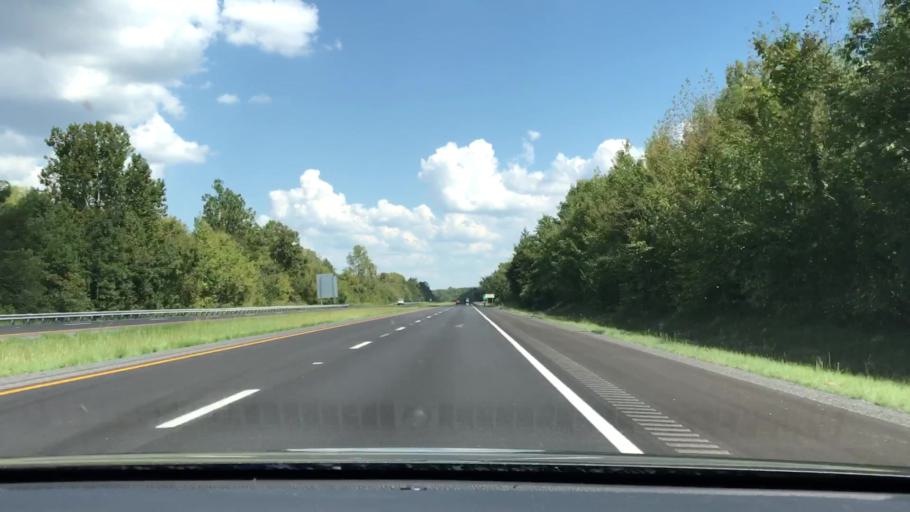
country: US
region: Kentucky
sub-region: Lyon County
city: Eddyville
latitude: 37.0898
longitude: -88.0560
